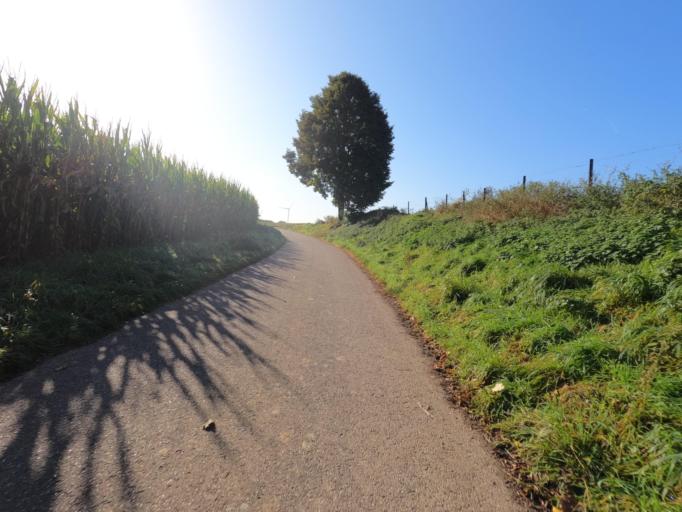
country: DE
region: North Rhine-Westphalia
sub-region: Regierungsbezirk Koln
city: Linnich
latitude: 51.0002
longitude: 6.2428
